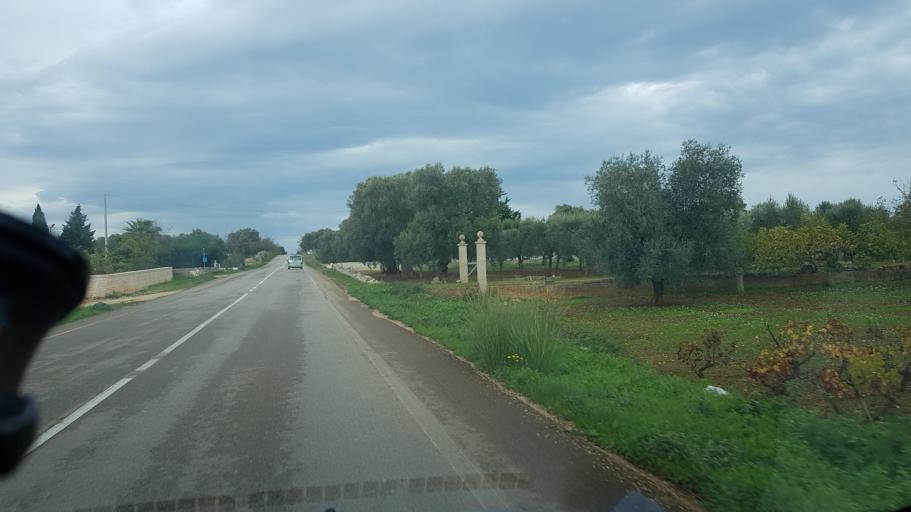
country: IT
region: Apulia
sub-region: Provincia di Brindisi
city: Carovigno
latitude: 40.6844
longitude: 17.6800
